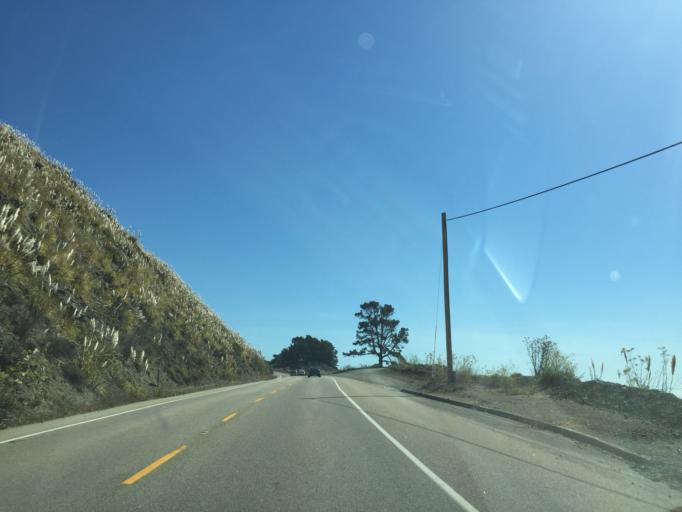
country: US
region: California
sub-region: Monterey County
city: Greenfield
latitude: 36.0335
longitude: -121.5768
